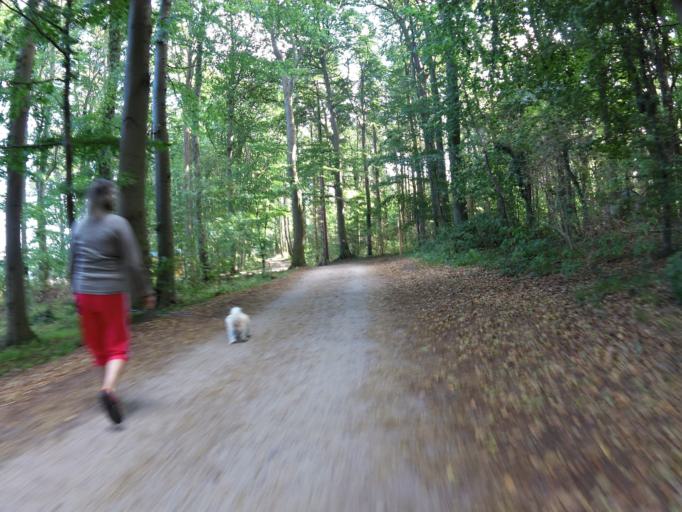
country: DE
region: Mecklenburg-Vorpommern
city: Koserow
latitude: 54.0477
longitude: 14.0208
